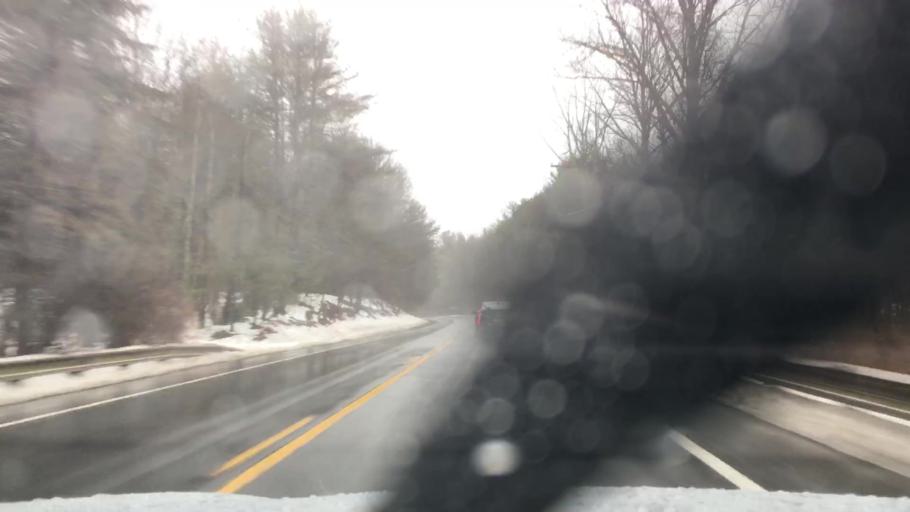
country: US
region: Massachusetts
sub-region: Franklin County
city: Shutesbury
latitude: 42.4845
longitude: -72.3426
